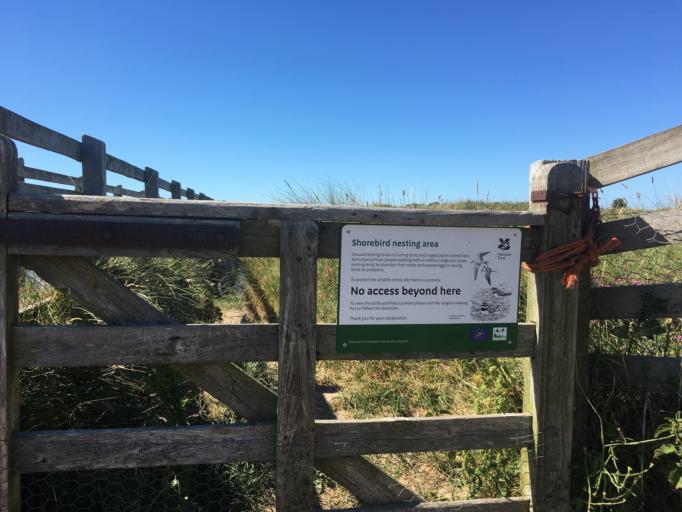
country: GB
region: England
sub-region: Northumberland
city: Beadnell
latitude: 55.5373
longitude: -1.6415
